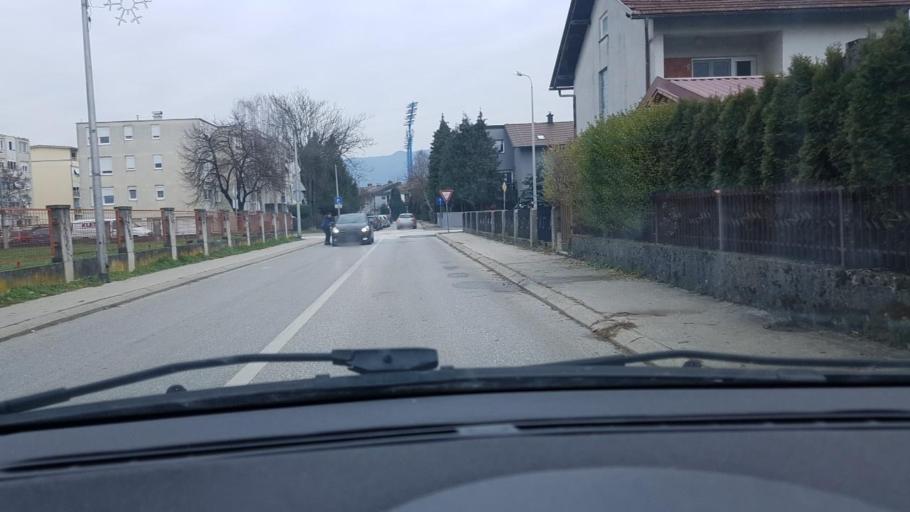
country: HR
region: Zagrebacka
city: Brdovec
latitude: 45.8656
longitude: 15.7958
